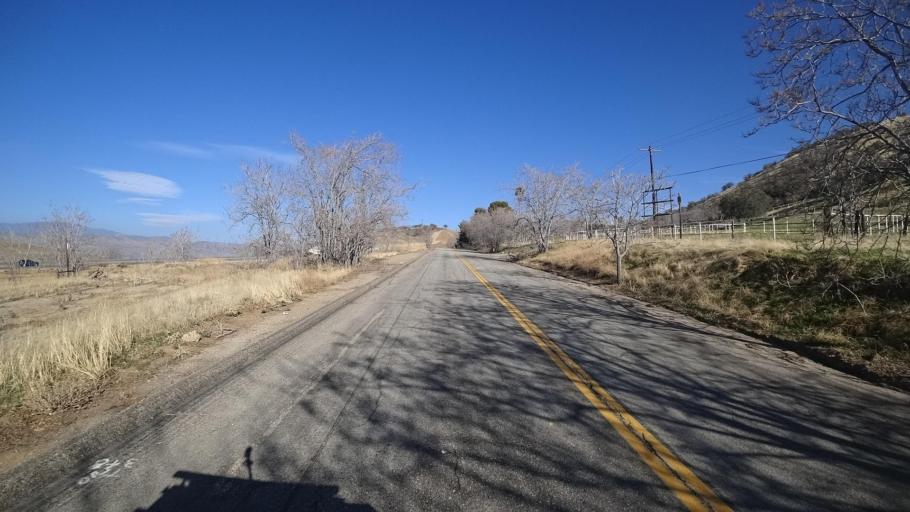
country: US
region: California
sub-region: Kern County
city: Bear Valley Springs
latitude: 35.2627
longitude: -118.6346
